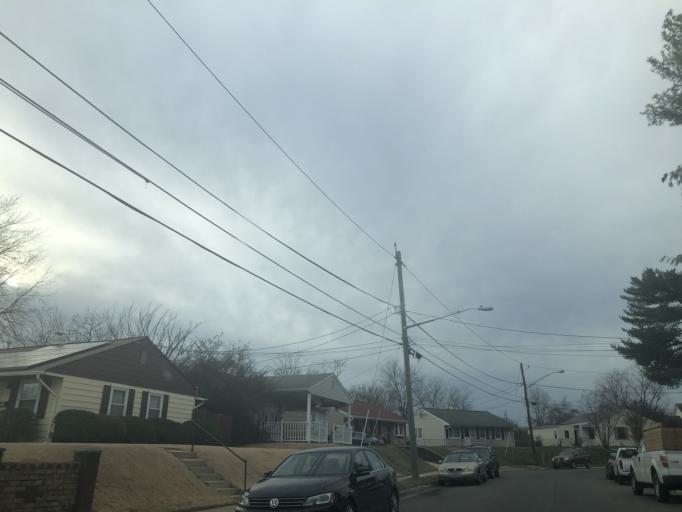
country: US
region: Maryland
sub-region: Prince George's County
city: Oxon Hill
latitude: 38.7932
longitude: -76.9956
